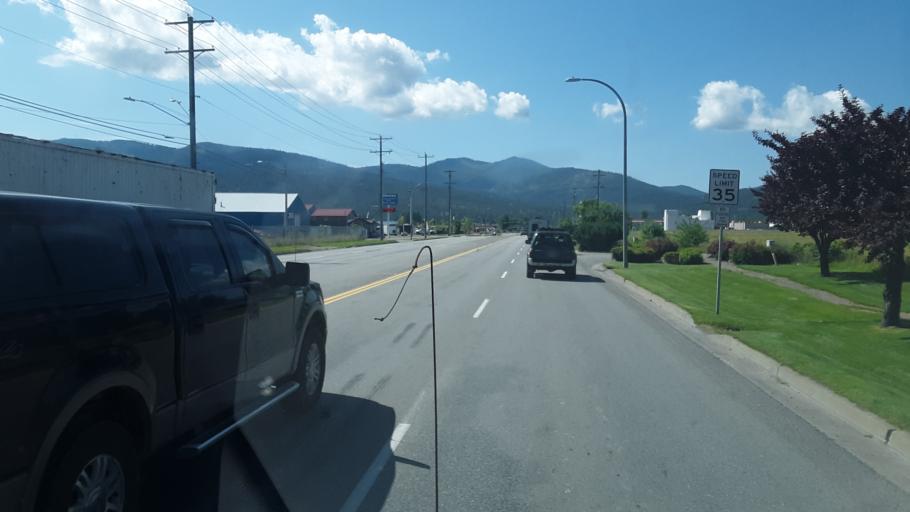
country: US
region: Idaho
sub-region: Kootenai County
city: Post Falls
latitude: 47.7160
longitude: -117.0018
